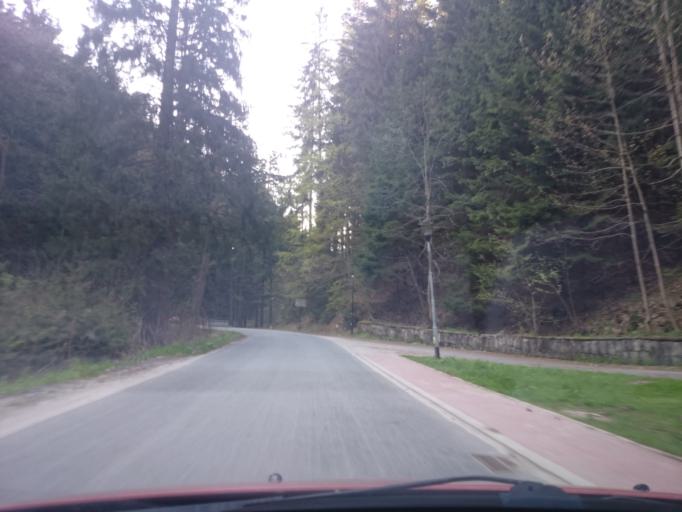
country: PL
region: Lower Silesian Voivodeship
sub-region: Powiat klodzki
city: Duszniki-Zdroj
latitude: 50.3802
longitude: 16.3908
